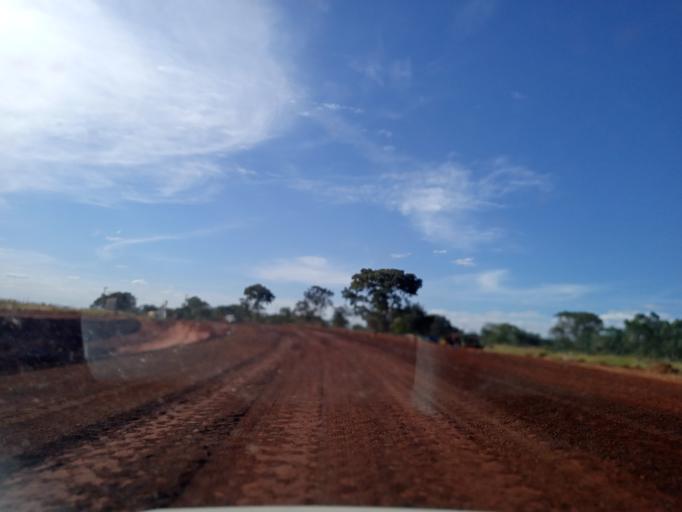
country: BR
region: Minas Gerais
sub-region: Ituiutaba
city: Ituiutaba
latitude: -18.9767
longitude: -49.5050
